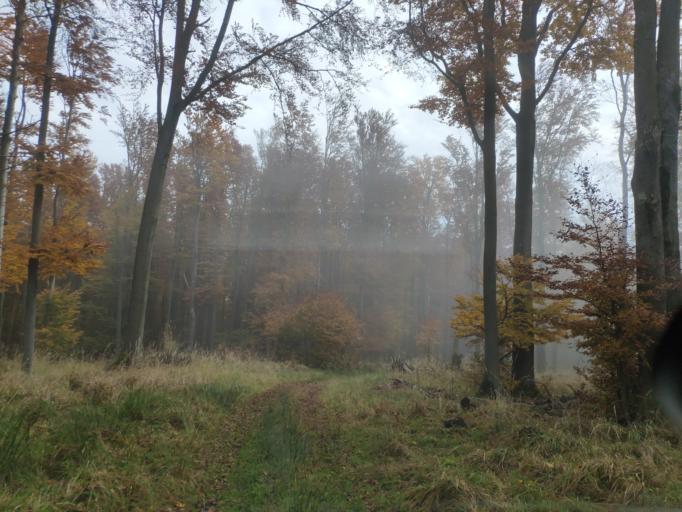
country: SK
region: Kosicky
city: Moldava nad Bodvou
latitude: 48.7324
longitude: 21.0117
